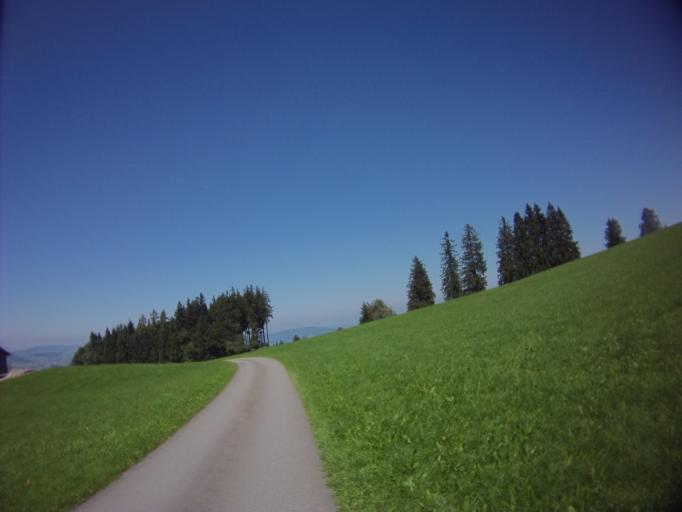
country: CH
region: Schwyz
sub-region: Bezirk Hoefe
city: Feusisberg
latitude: 47.1756
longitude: 8.7526
